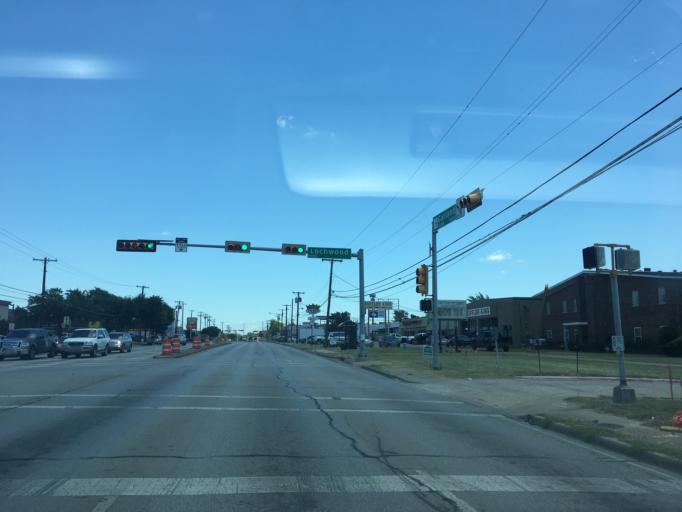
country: US
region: Texas
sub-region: Dallas County
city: Garland
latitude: 32.8469
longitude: -96.6861
